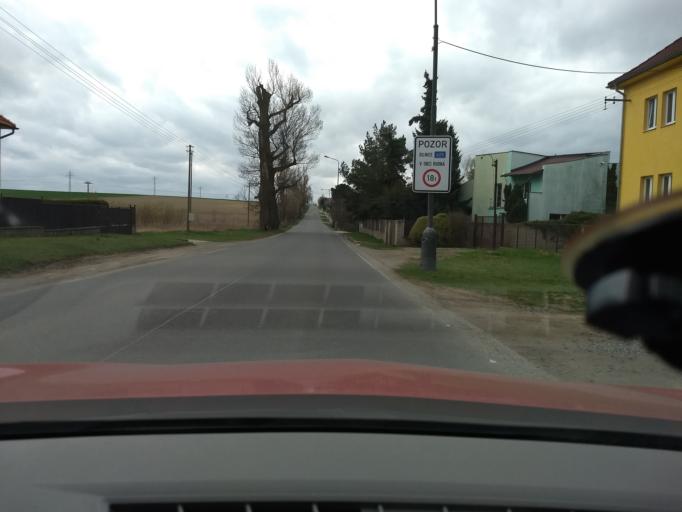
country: CZ
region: Central Bohemia
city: Unhost'
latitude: 50.0850
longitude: 14.1389
